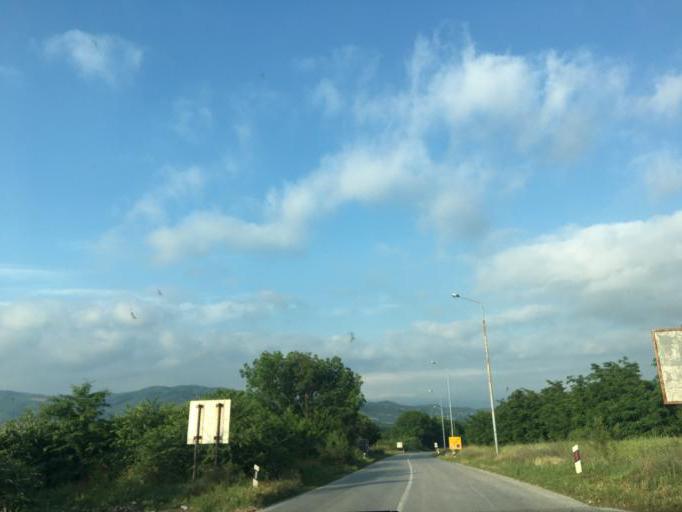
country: MK
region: Valandovo
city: Valandovo
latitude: 41.3149
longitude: 22.5563
